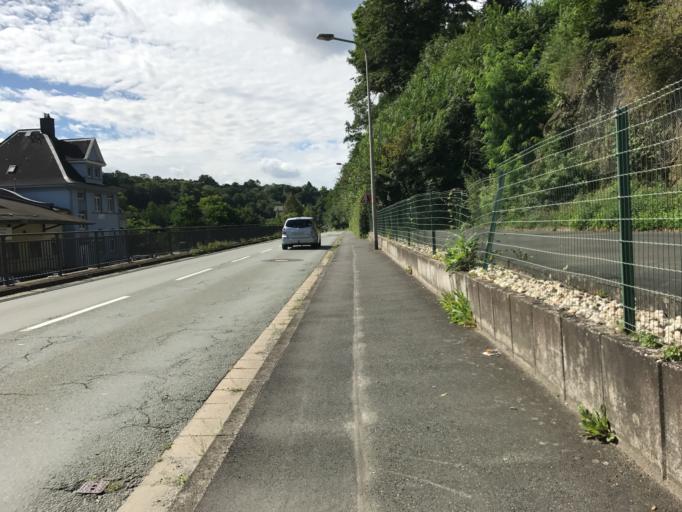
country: DE
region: Hesse
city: Weilburg
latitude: 50.4890
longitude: 8.2683
